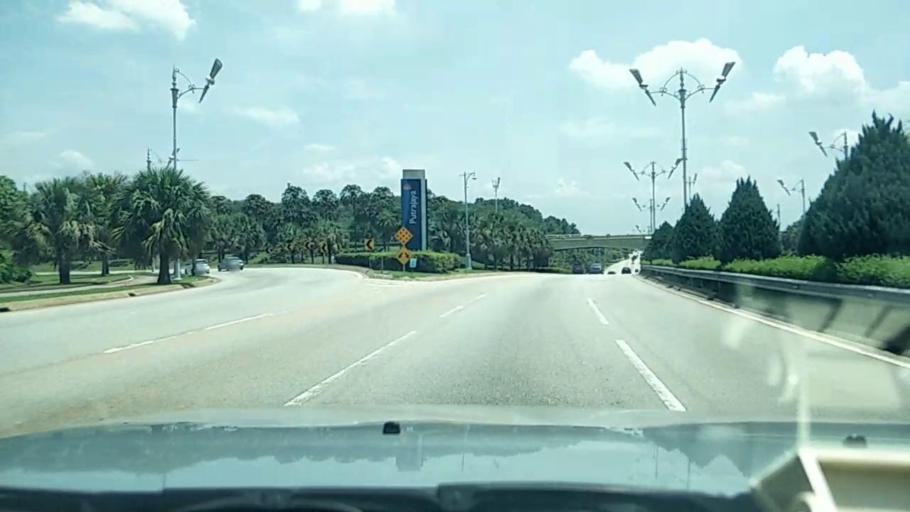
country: MY
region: Putrajaya
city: Putrajaya
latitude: 2.9580
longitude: 101.7150
